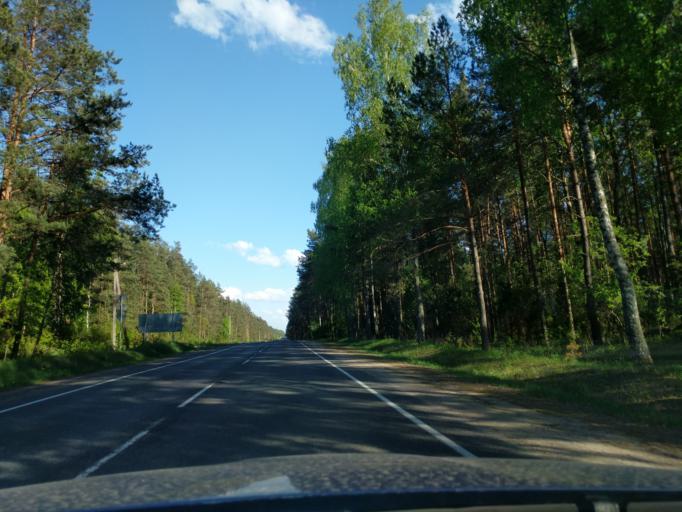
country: BY
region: Minsk
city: Myadzyel
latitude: 54.8260
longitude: 26.9463
